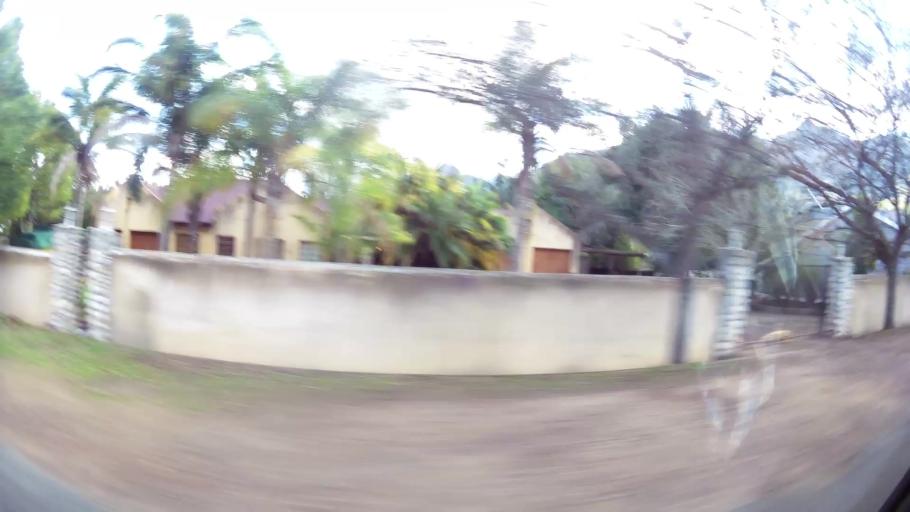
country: ZA
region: Western Cape
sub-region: Overberg District Municipality
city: Swellendam
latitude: -34.0120
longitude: 20.4578
